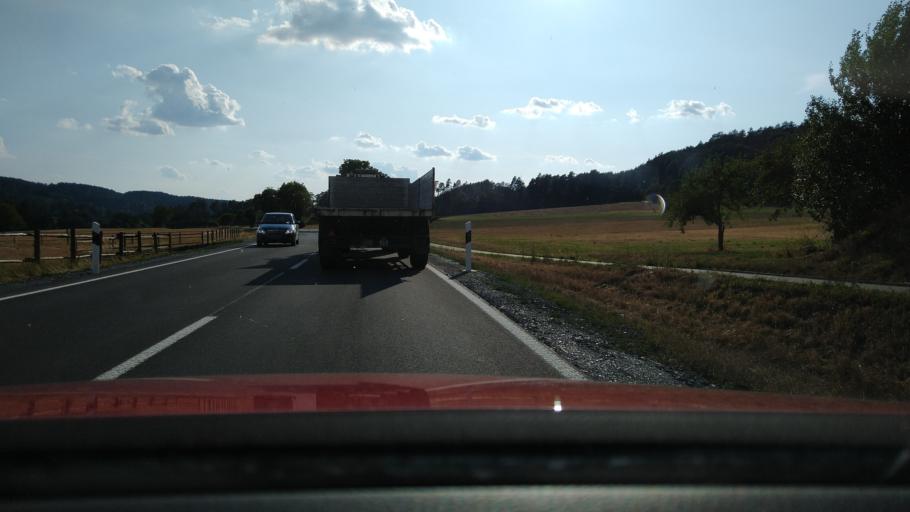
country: DE
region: Bavaria
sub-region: Upper Franconia
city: Mistelgau
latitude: 49.9266
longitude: 11.4442
